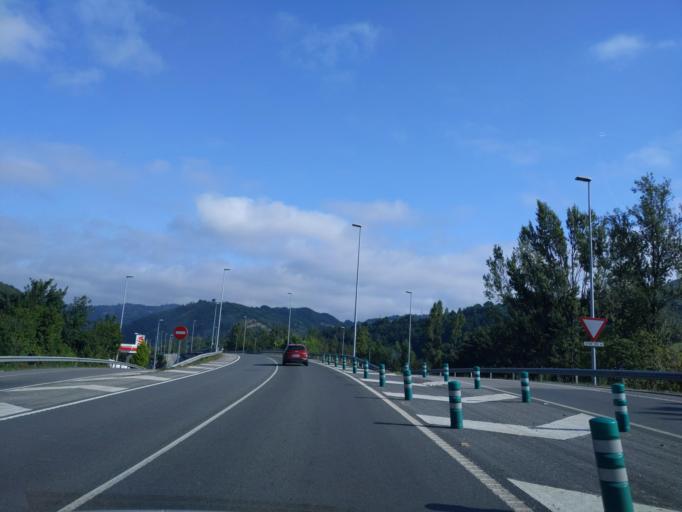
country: ES
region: Asturias
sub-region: Province of Asturias
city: Pola de Laviana
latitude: 43.2483
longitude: -5.5677
